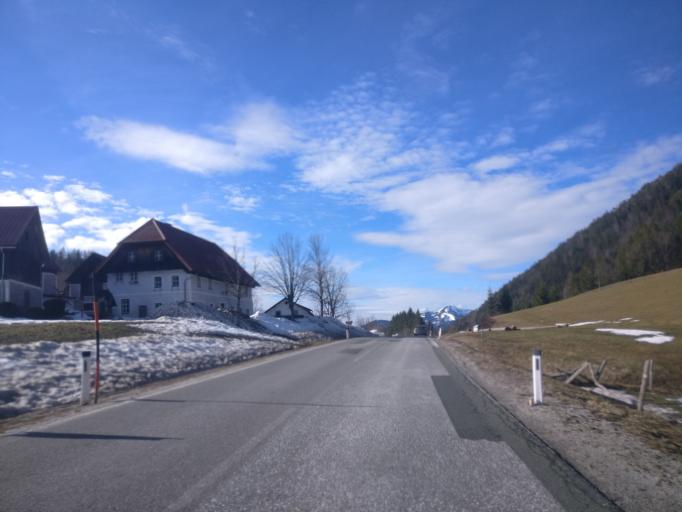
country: AT
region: Styria
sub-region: Politischer Bezirk Liezen
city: Landl
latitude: 47.6565
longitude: 14.6610
